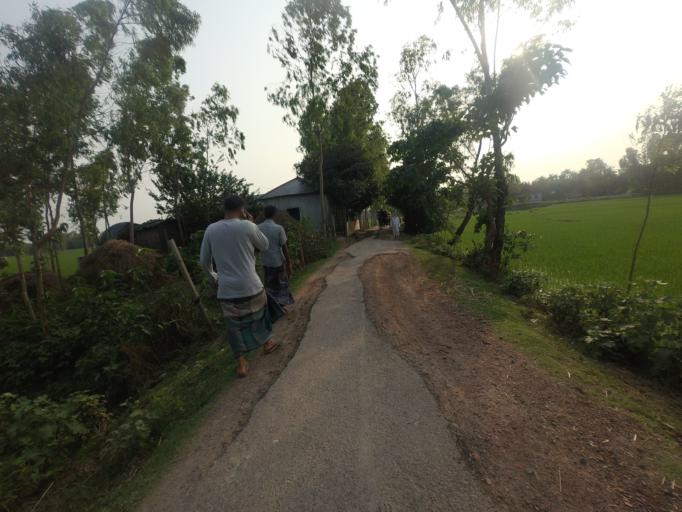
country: BD
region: Rajshahi
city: Sirajganj
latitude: 24.3212
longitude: 89.7019
